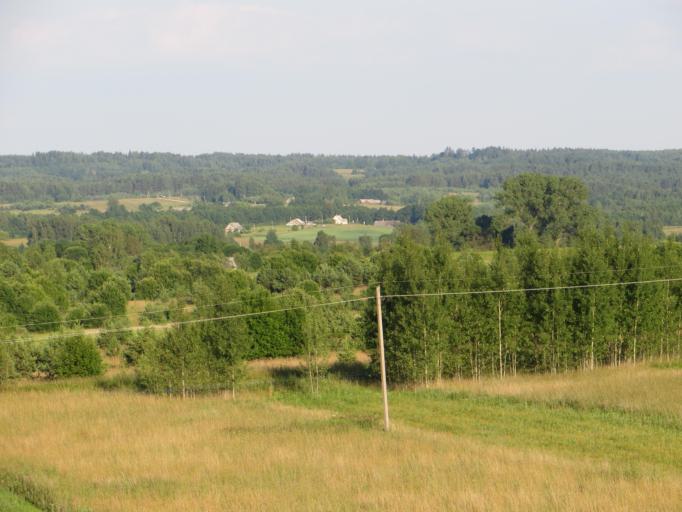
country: LT
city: Svencionys
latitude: 55.2291
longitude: 26.1842
